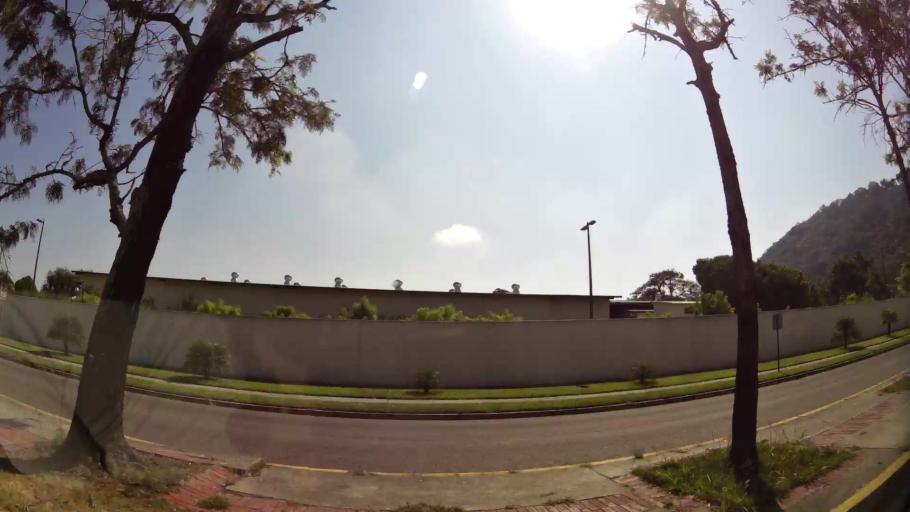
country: SV
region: La Libertad
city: Antiguo Cuscatlan
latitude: 13.6639
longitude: -89.2587
